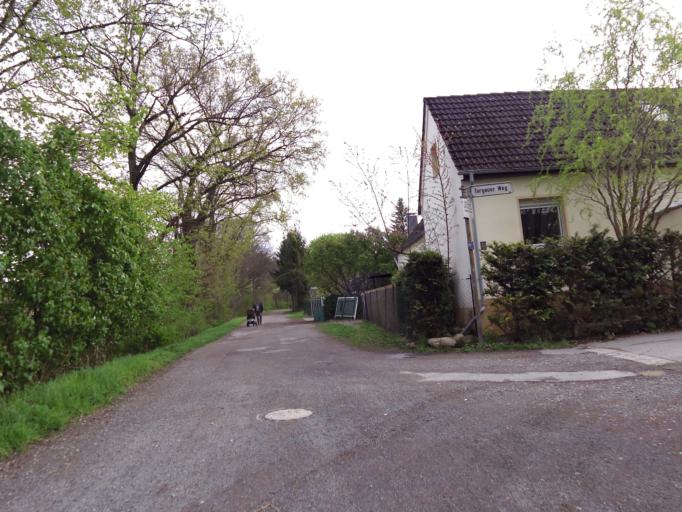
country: DE
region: Lower Saxony
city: Laatzen
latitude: 52.3860
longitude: 9.8353
